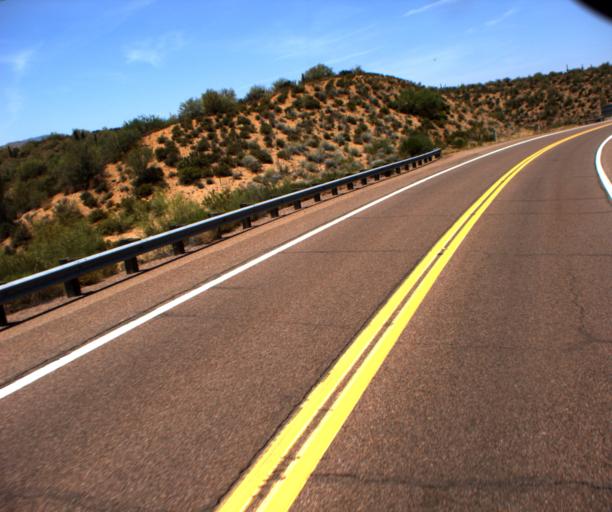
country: US
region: Arizona
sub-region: Gila County
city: Tonto Basin
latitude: 33.6999
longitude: -111.1884
